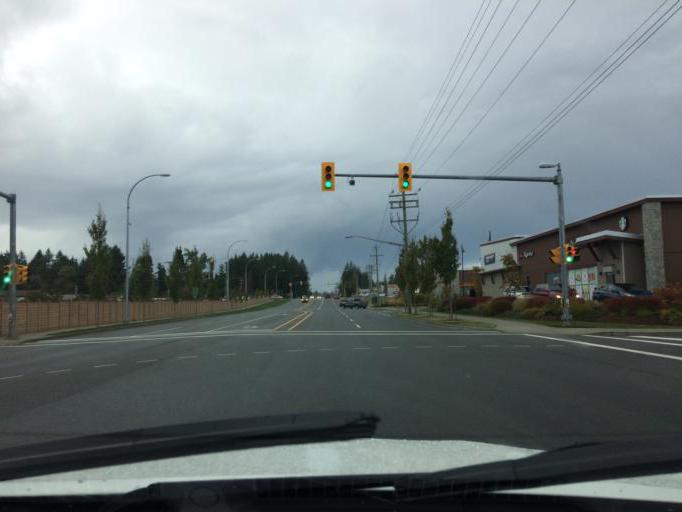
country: CA
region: British Columbia
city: Courtenay
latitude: 49.7085
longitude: -124.9632
